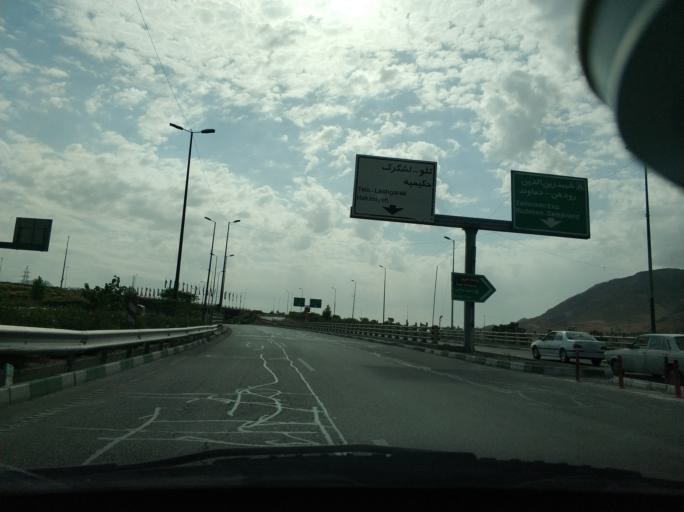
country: IR
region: Tehran
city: Tehran
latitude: 35.7236
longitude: 51.5835
